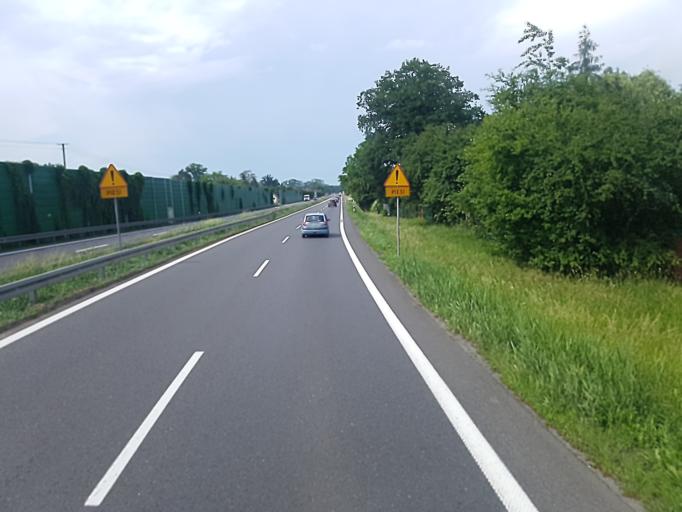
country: PL
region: Silesian Voivodeship
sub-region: Powiat cieszynski
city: Ochaby
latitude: 49.8462
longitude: 18.7638
